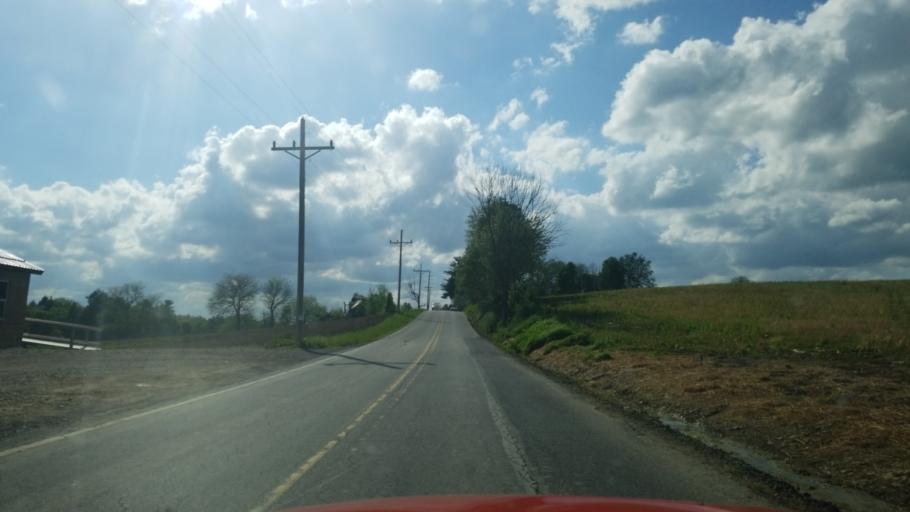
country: US
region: Pennsylvania
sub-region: Clearfield County
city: Hyde
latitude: 40.9771
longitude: -78.4670
